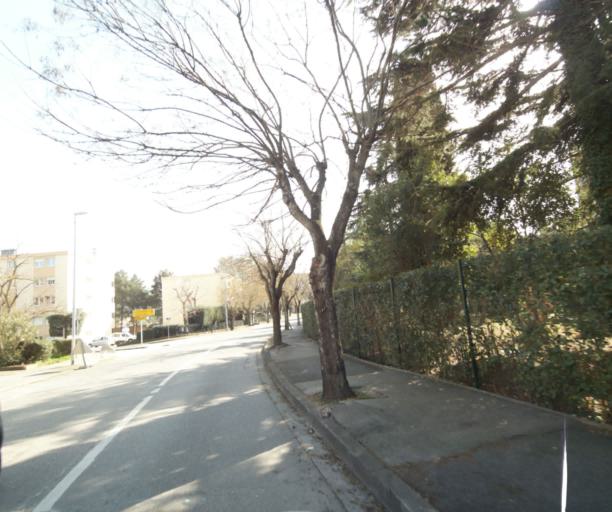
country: FR
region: Provence-Alpes-Cote d'Azur
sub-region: Departement des Bouches-du-Rhone
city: Aix-en-Provence
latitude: 43.5138
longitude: 5.4635
